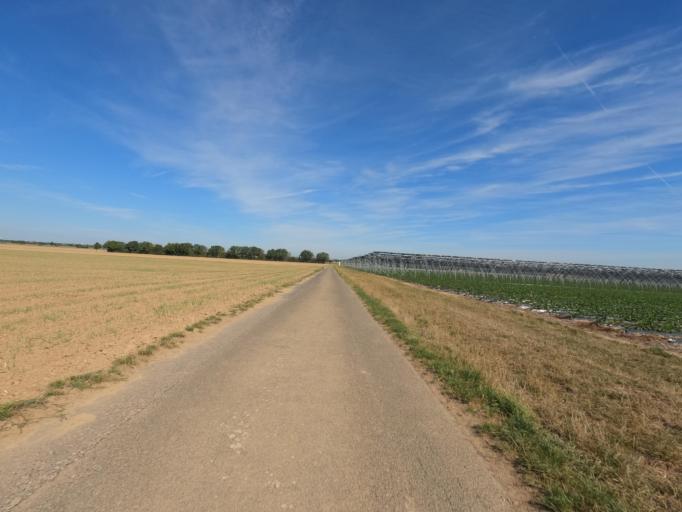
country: DE
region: North Rhine-Westphalia
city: Erkelenz
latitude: 51.0448
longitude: 6.3542
